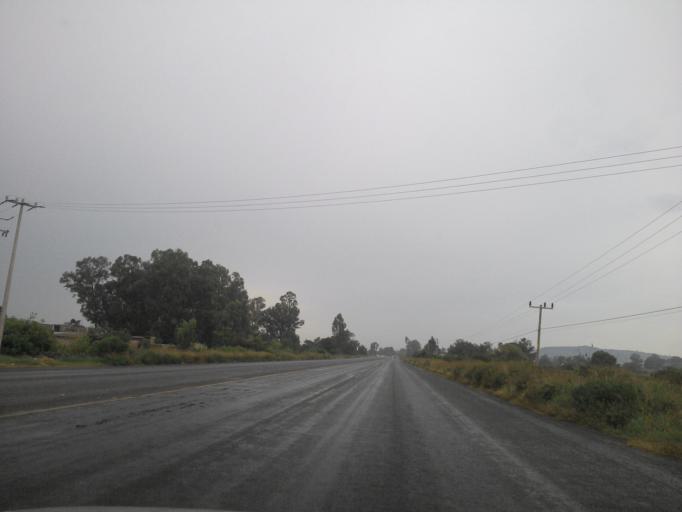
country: MX
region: Jalisco
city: Capilla de Guadalupe
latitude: 20.8478
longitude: -102.6123
